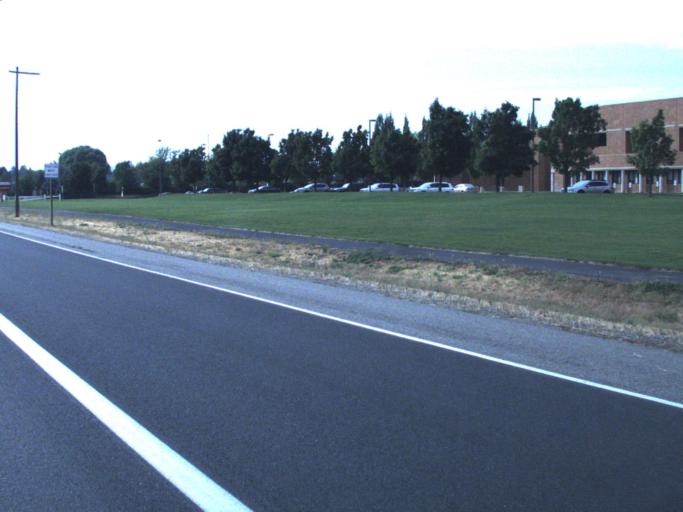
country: US
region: Washington
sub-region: Spokane County
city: Mead
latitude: 47.7874
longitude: -117.3219
